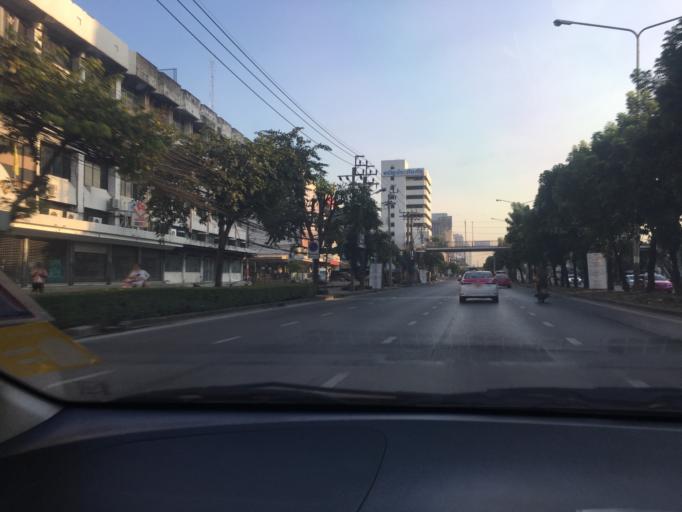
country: TH
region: Bangkok
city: Huai Khwang
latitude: 13.7980
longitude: 100.5746
